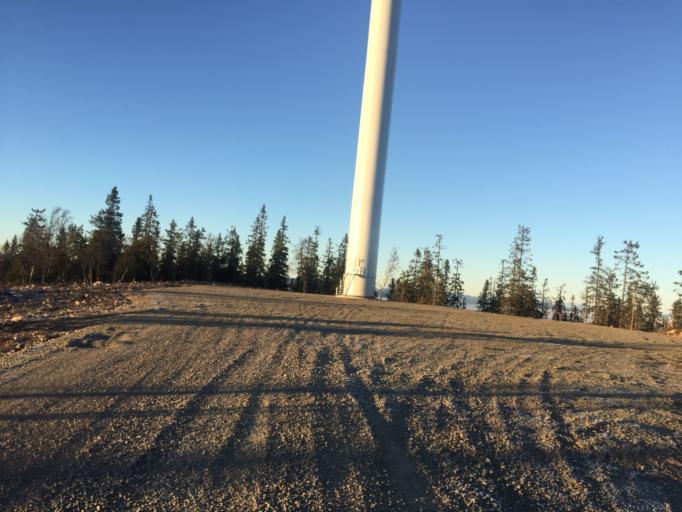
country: NO
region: Hedmark
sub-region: Elverum
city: Elverum
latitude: 61.2133
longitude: 11.7787
